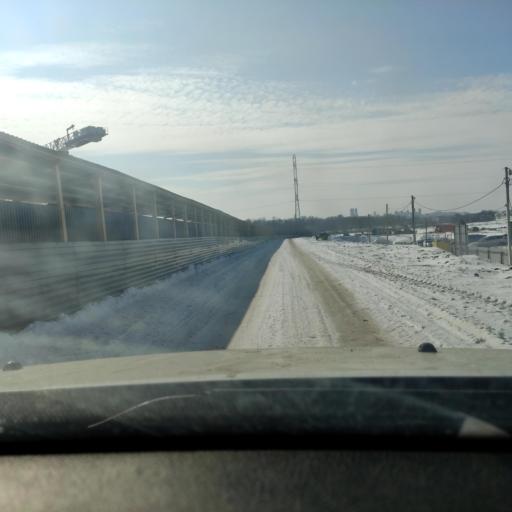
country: RU
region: Bashkortostan
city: Ufa
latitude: 54.7801
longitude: 55.9607
